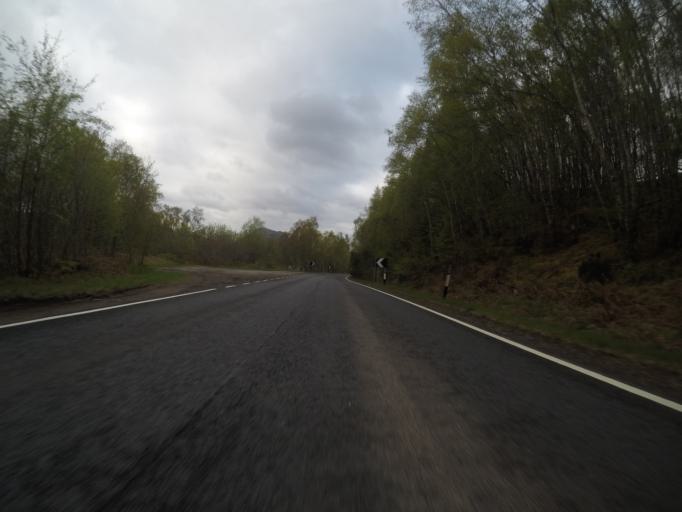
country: GB
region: Scotland
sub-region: Highland
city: Kingussie
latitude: 56.9664
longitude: -4.4438
